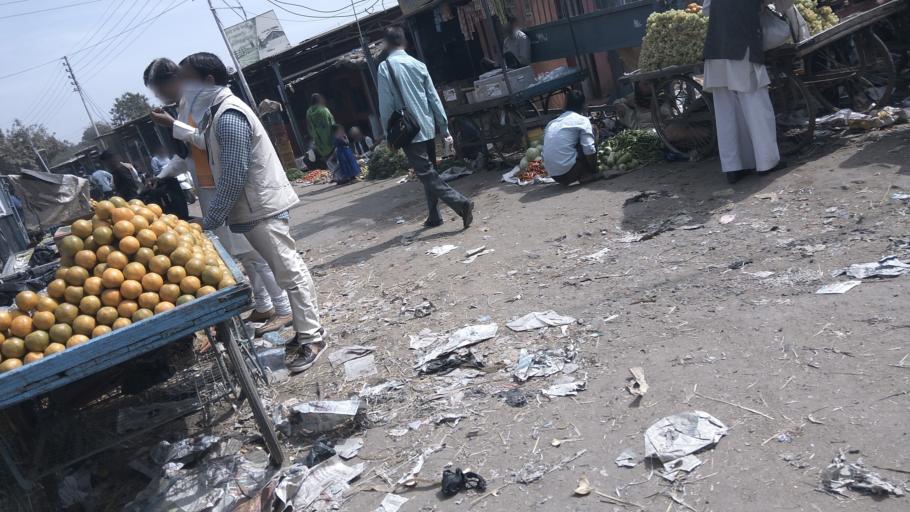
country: IN
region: Uttar Pradesh
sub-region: Jhansi
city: Jhansi
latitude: 25.4466
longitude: 78.5914
